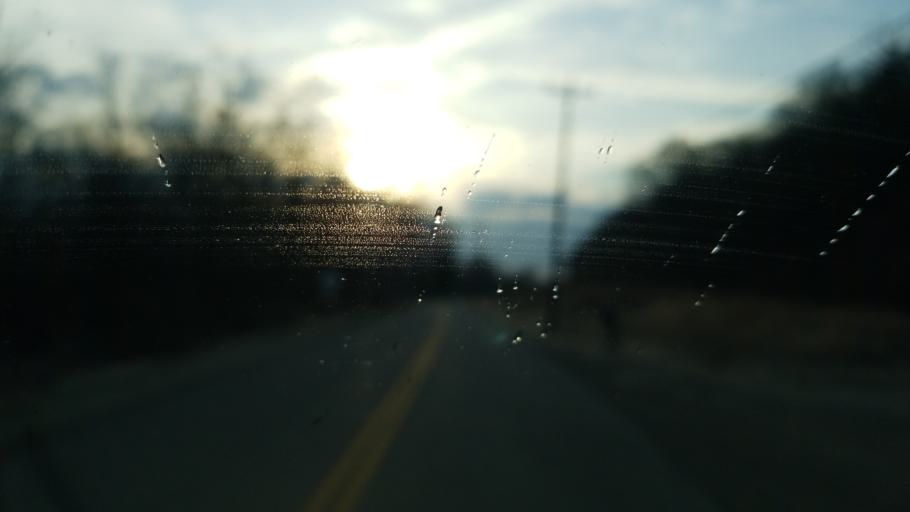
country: US
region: Ohio
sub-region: Ross County
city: Chillicothe
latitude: 39.2818
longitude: -82.9353
